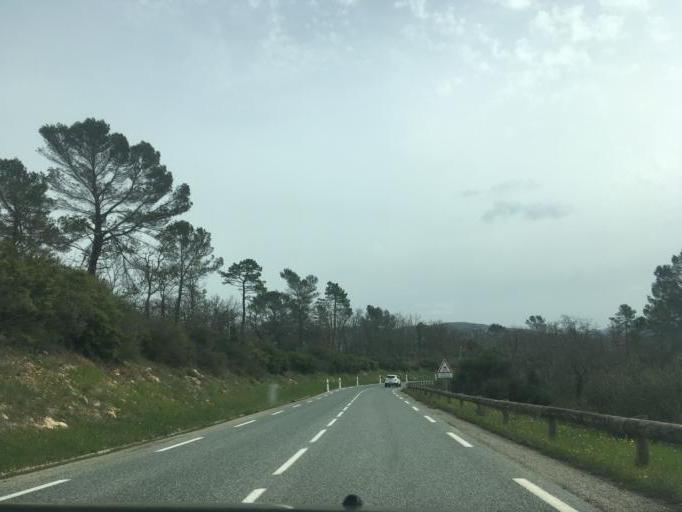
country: FR
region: Provence-Alpes-Cote d'Azur
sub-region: Departement du Var
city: Callian
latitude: 43.5922
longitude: 6.7385
